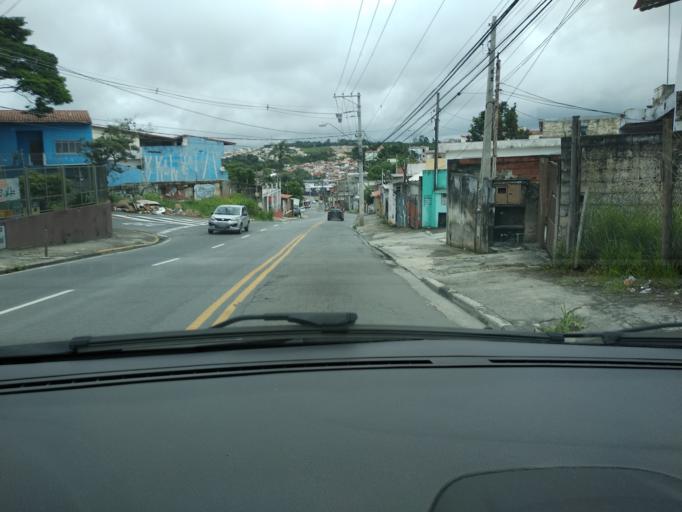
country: BR
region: Sao Paulo
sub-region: Mogi das Cruzes
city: Mogi das Cruzes
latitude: -23.5405
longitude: -46.1823
